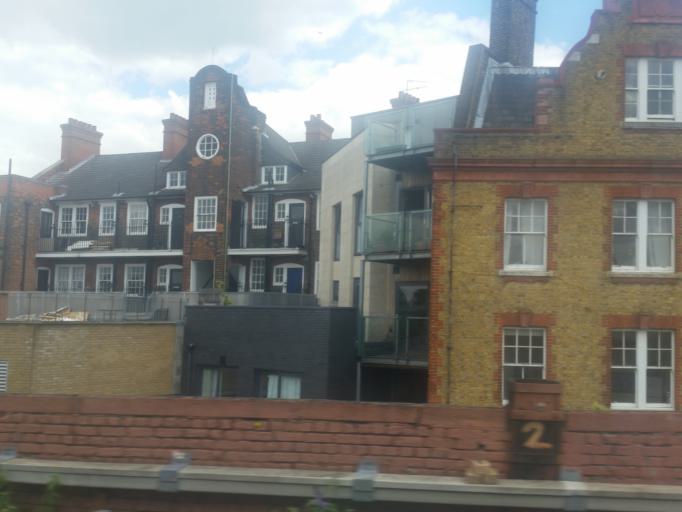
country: GB
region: England
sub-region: Greater London
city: Brixton
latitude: 51.4531
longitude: -0.1017
